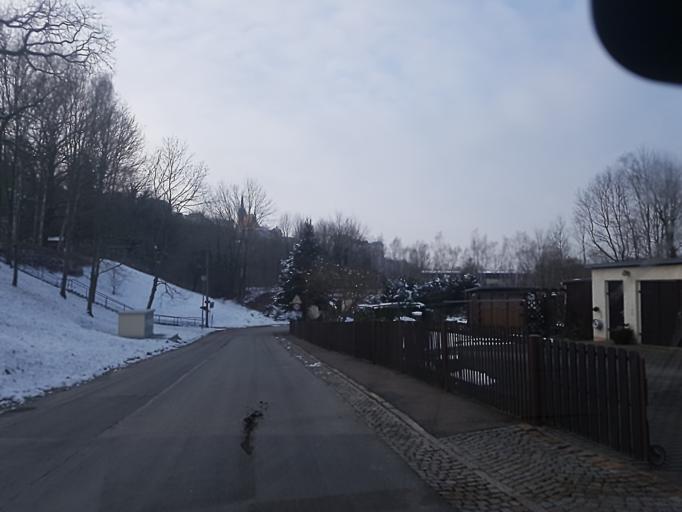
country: DE
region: Saxony
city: Leisnig
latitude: 51.1598
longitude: 12.9354
